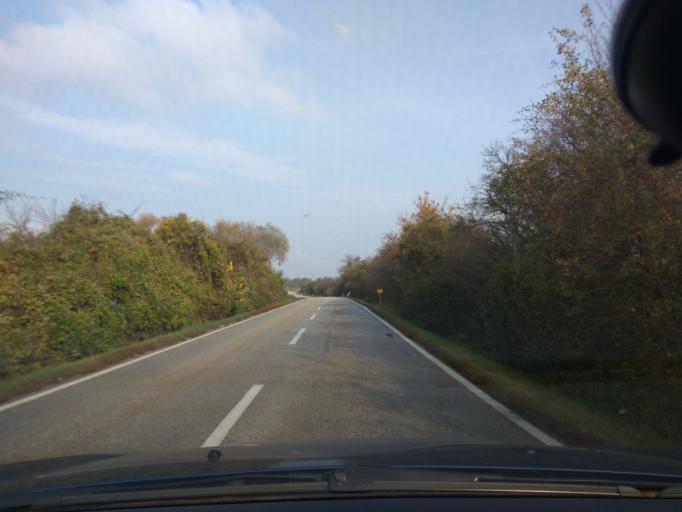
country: SK
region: Trnavsky
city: Vrbove
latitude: 48.6526
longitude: 17.7545
